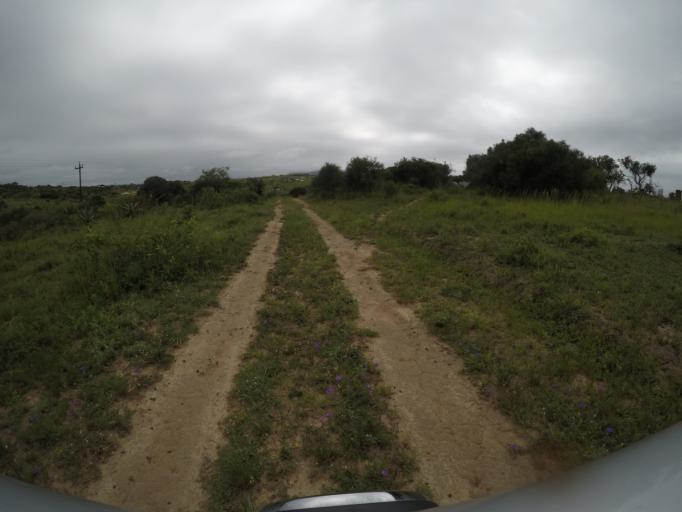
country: ZA
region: KwaZulu-Natal
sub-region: uThungulu District Municipality
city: Empangeni
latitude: -28.6076
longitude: 31.8370
